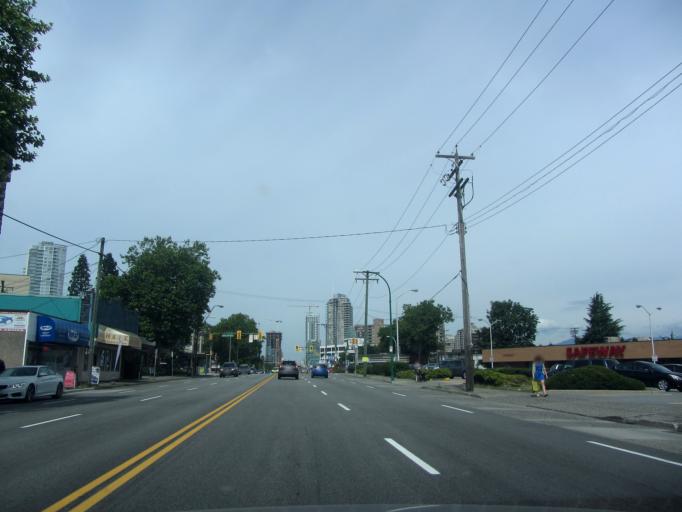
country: CA
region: British Columbia
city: Burnaby
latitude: 49.2190
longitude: -122.9671
